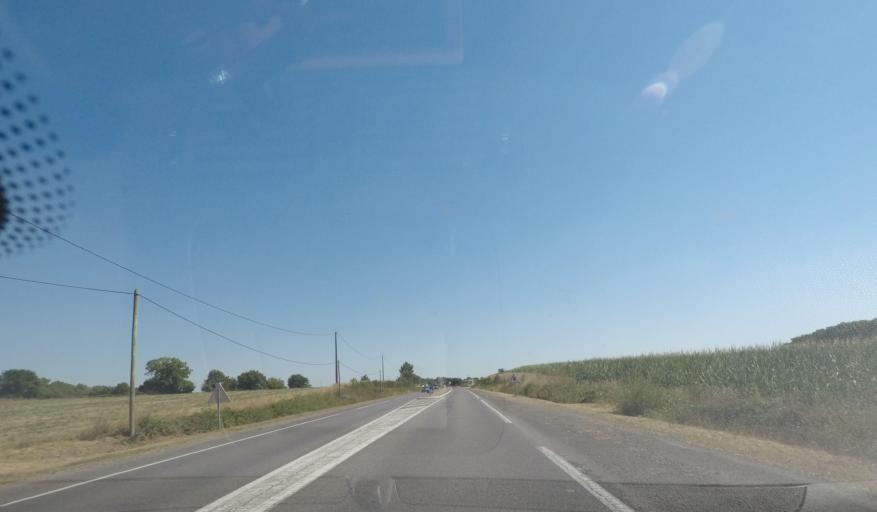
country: FR
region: Brittany
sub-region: Departement du Morbihan
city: Limerzel
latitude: 47.6242
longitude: -2.4077
